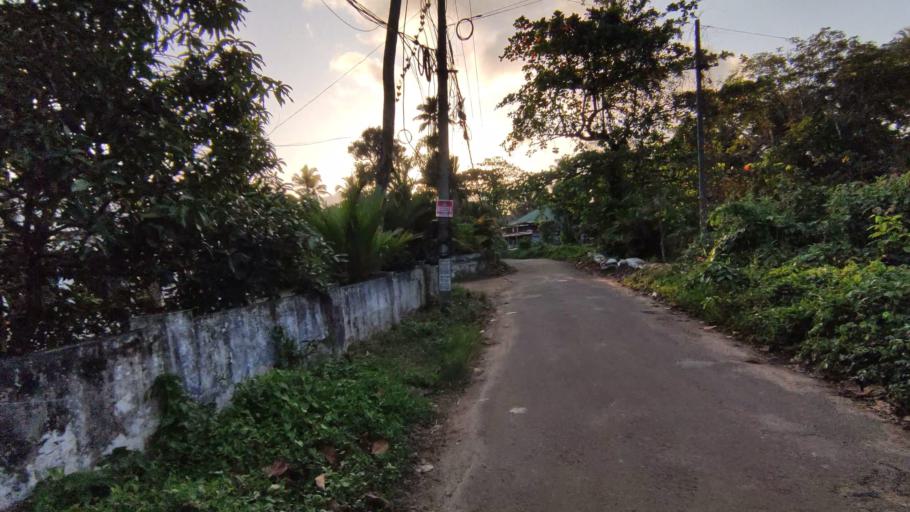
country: IN
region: Kerala
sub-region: Kottayam
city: Kottayam
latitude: 9.5958
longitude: 76.4655
